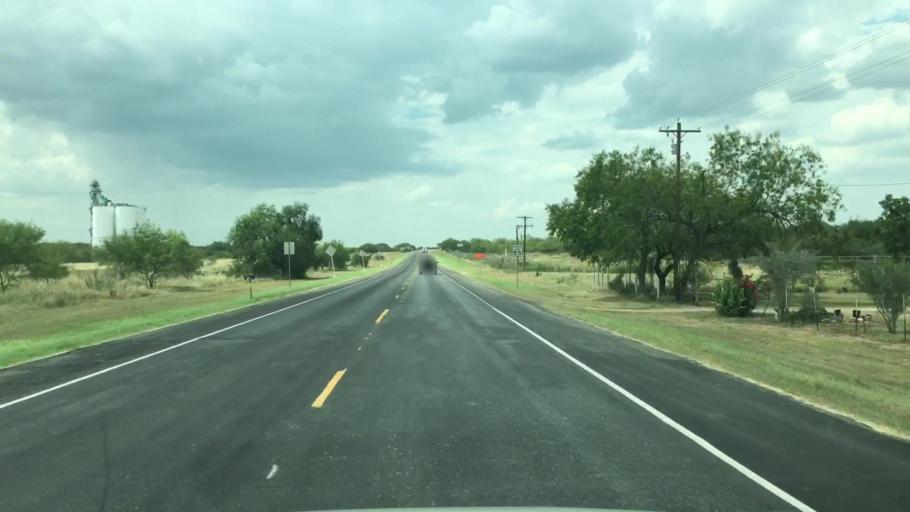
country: US
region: Texas
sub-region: Live Oak County
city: Three Rivers
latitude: 28.6362
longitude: -98.2754
